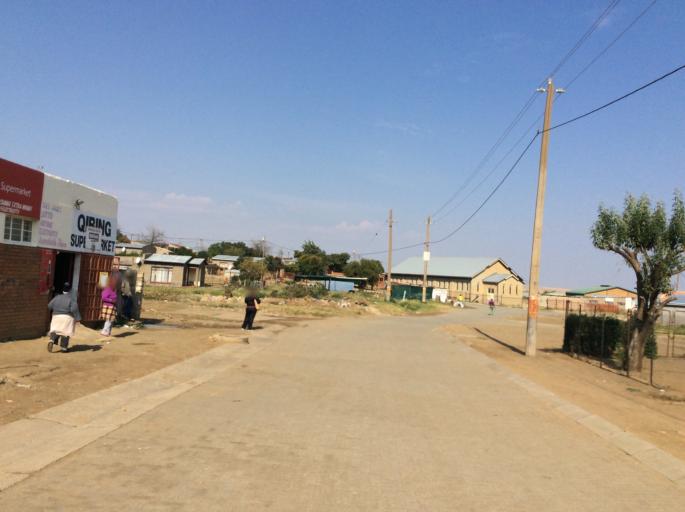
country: LS
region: Mafeteng
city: Mafeteng
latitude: -29.7183
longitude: 27.0291
